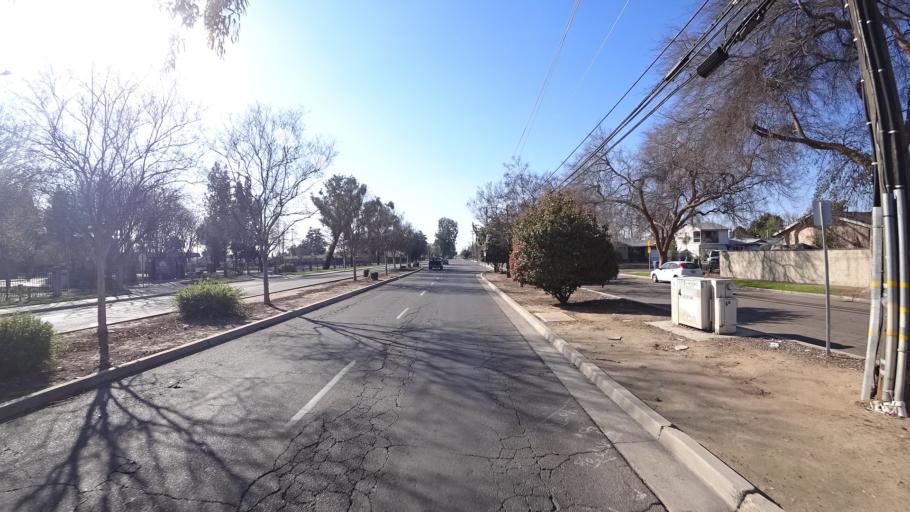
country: US
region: California
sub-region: Fresno County
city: Fresno
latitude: 36.7264
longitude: -119.7366
